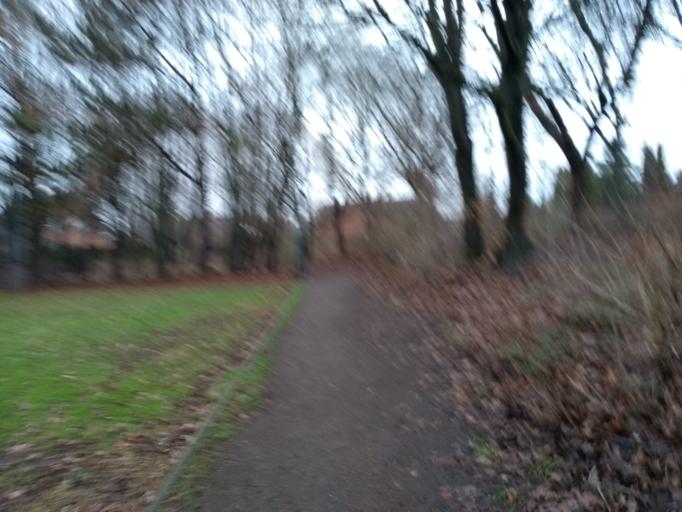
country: DE
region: North Rhine-Westphalia
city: Selm
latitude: 51.6896
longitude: 7.4586
